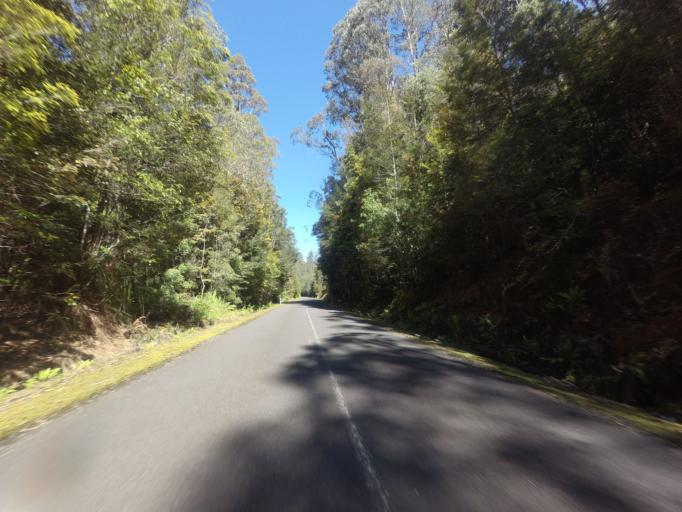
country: AU
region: Tasmania
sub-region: Huon Valley
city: Geeveston
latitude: -42.8253
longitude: 146.3159
